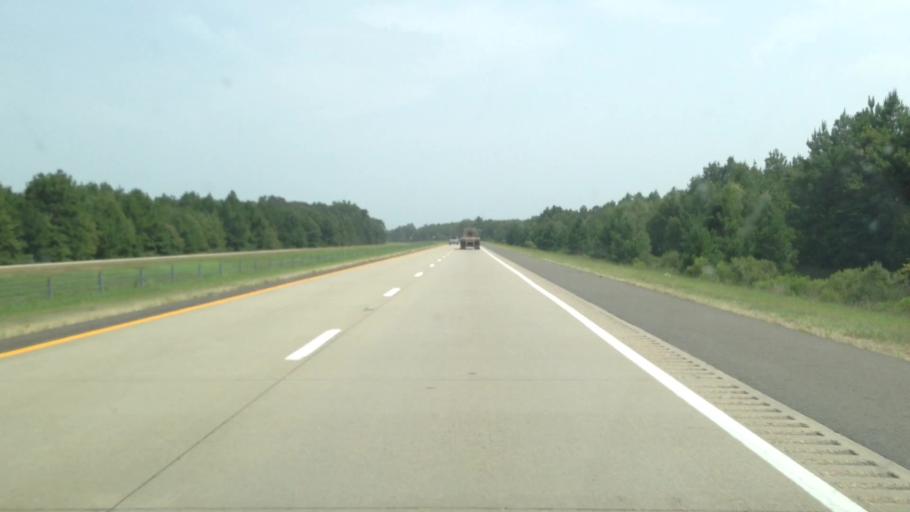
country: US
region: Texas
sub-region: Bowie County
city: Texarkana
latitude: 33.2054
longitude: -93.8759
